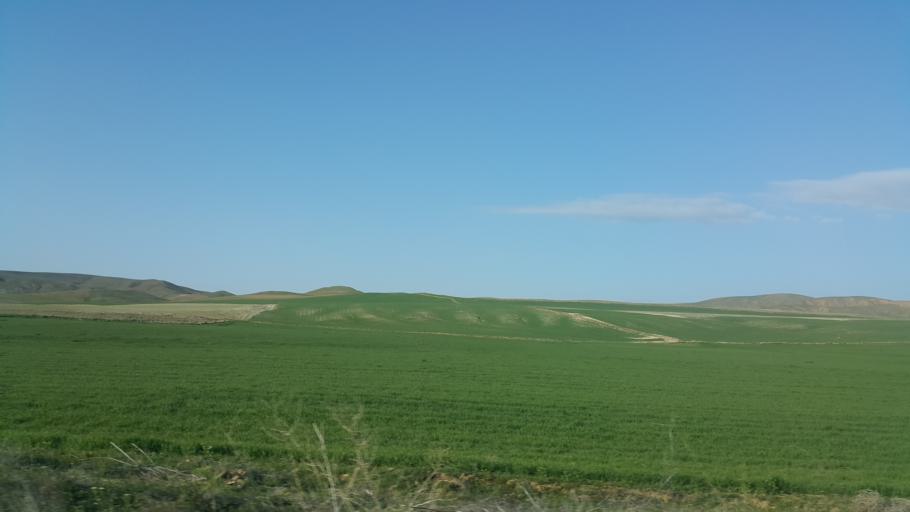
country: TR
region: Ankara
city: Sereflikochisar
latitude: 39.1150
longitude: 33.3593
